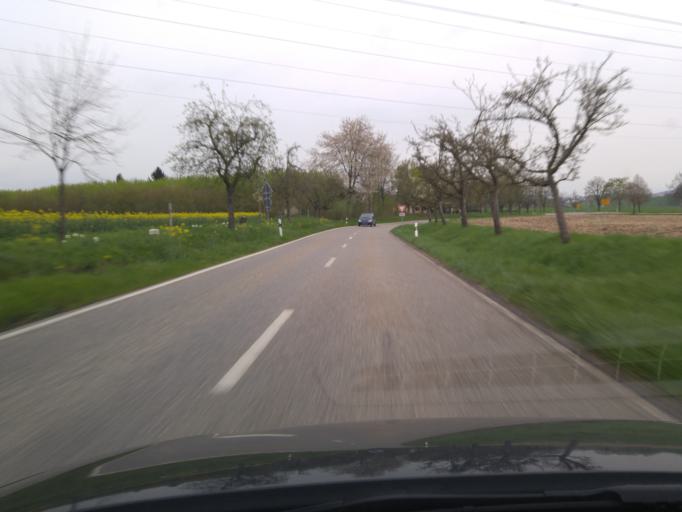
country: DE
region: Baden-Wuerttemberg
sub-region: Regierungsbezirk Stuttgart
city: Bad Rappenau
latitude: 49.2517
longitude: 9.1160
